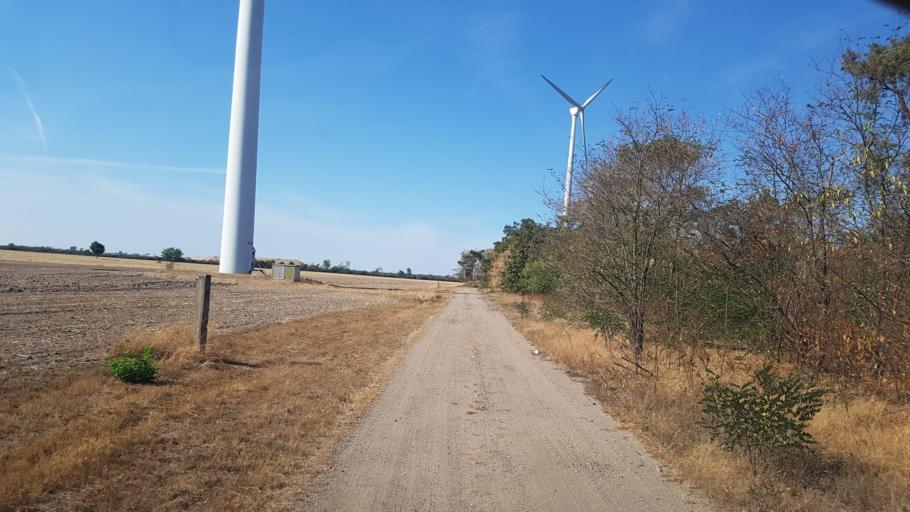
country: DE
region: Brandenburg
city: Muhlberg
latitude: 51.4093
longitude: 13.2850
